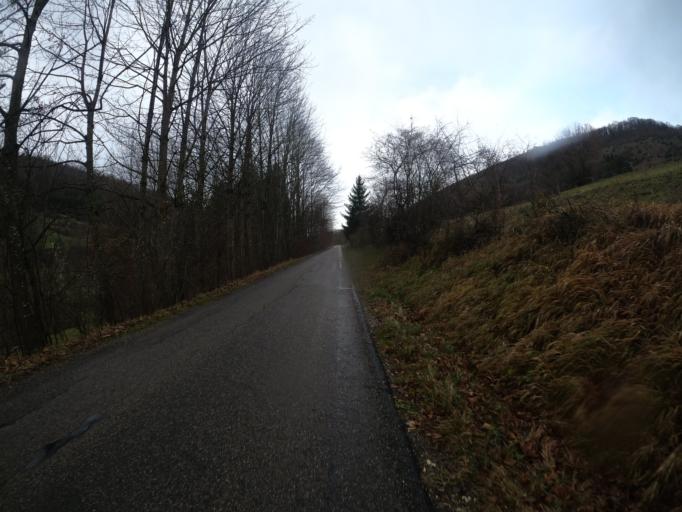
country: DE
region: Baden-Wuerttemberg
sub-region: Regierungsbezirk Stuttgart
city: Donzdorf
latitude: 48.7203
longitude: 9.8526
